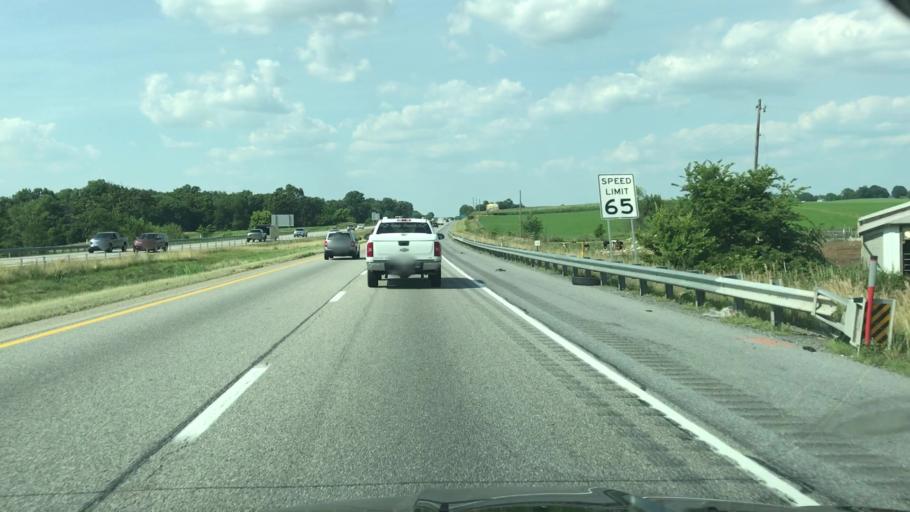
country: US
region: Pennsylvania
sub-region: Franklin County
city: Greencastle
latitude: 39.7971
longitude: -77.7101
